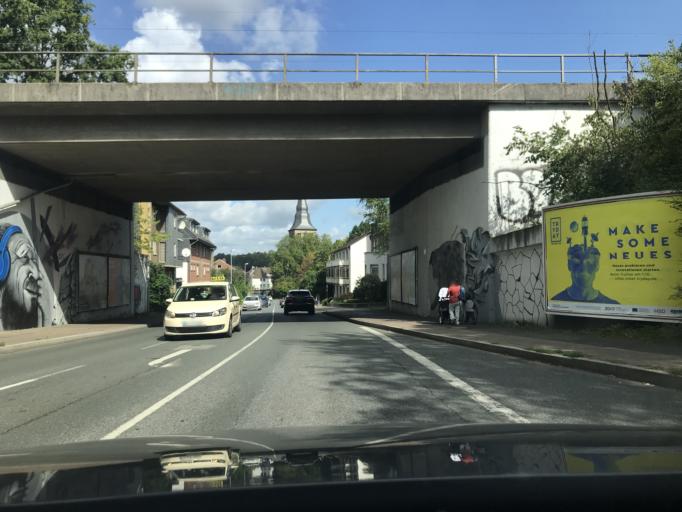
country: DE
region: North Rhine-Westphalia
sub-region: Regierungsbezirk Dusseldorf
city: Erkrath
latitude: 51.2198
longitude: 6.9130
